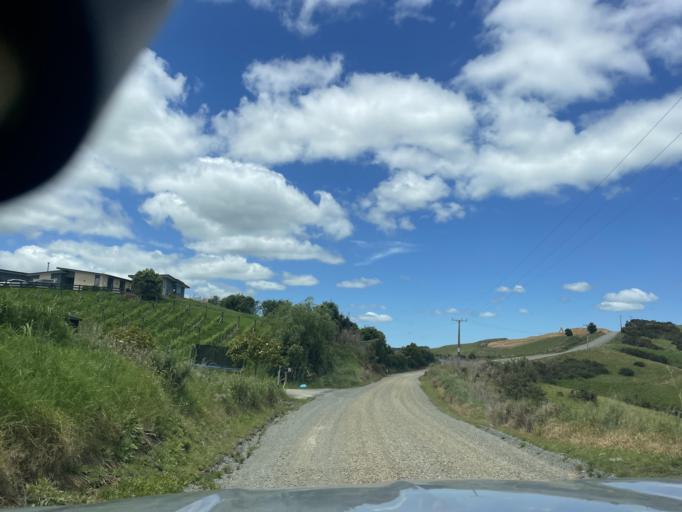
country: NZ
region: Auckland
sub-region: Auckland
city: Wellsford
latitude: -36.1554
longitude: 174.5427
